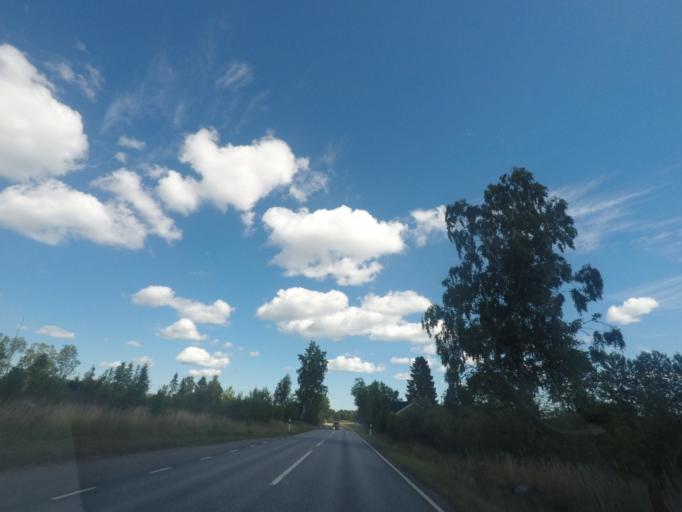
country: SE
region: Stockholm
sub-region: Norrtalje Kommun
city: Hallstavik
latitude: 59.9433
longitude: 18.7518
